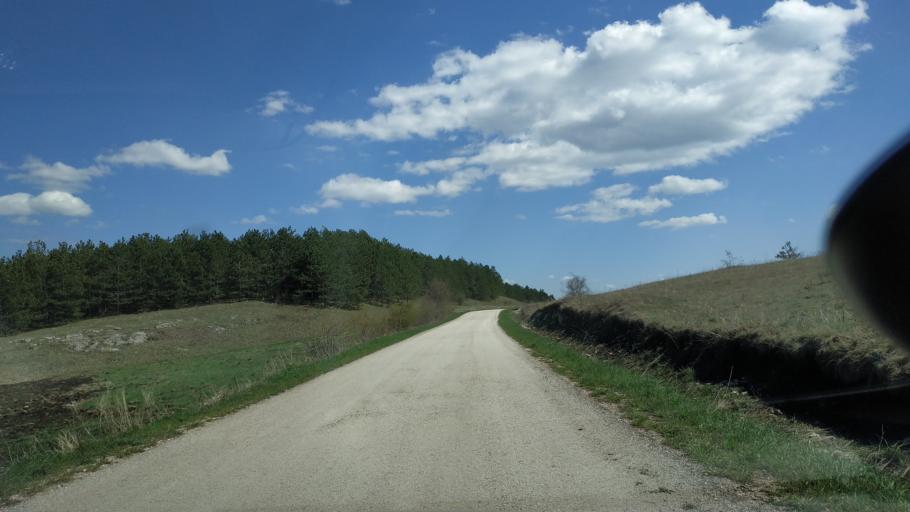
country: RS
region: Central Serbia
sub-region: Zajecarski Okrug
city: Soko Banja
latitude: 43.5933
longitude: 21.8856
